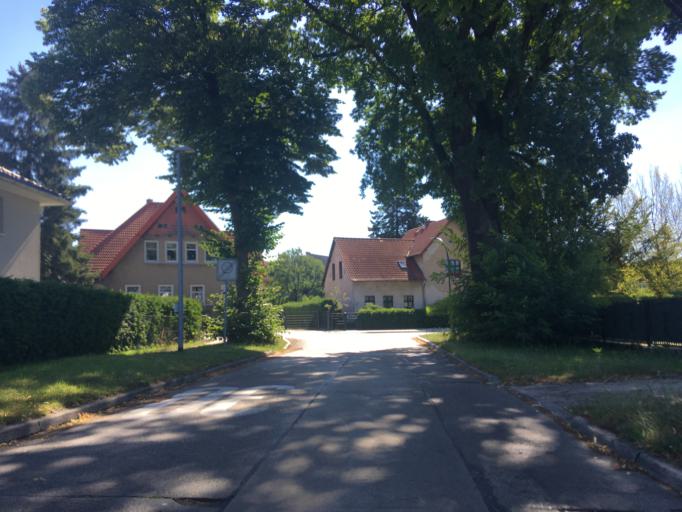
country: DE
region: Brandenburg
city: Petershagen
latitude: 52.5299
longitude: 13.7546
